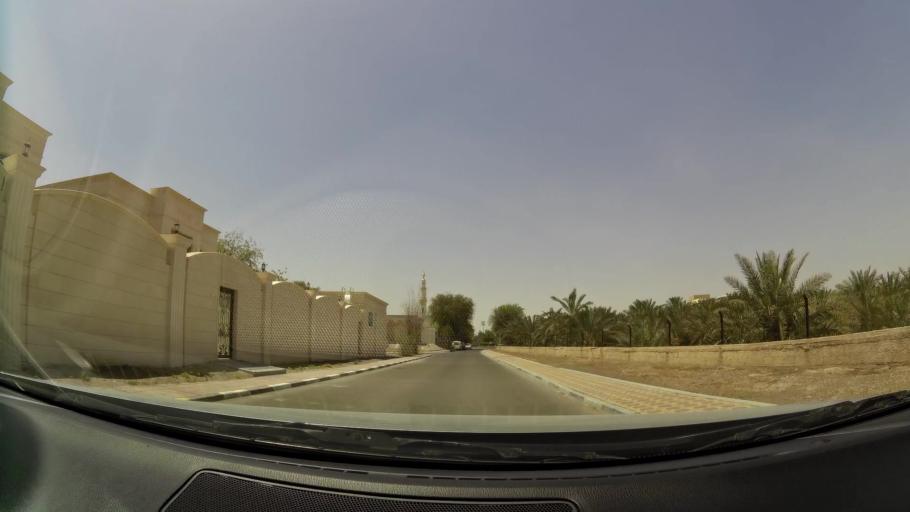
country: OM
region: Al Buraimi
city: Al Buraymi
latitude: 24.2748
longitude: 55.7553
